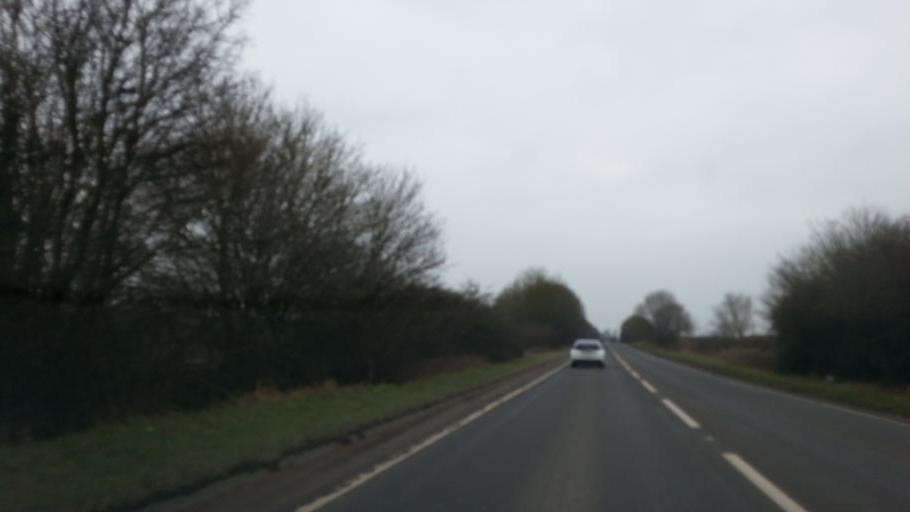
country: GB
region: England
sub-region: District of Rutland
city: South Luffenham
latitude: 52.5627
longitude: -0.5735
